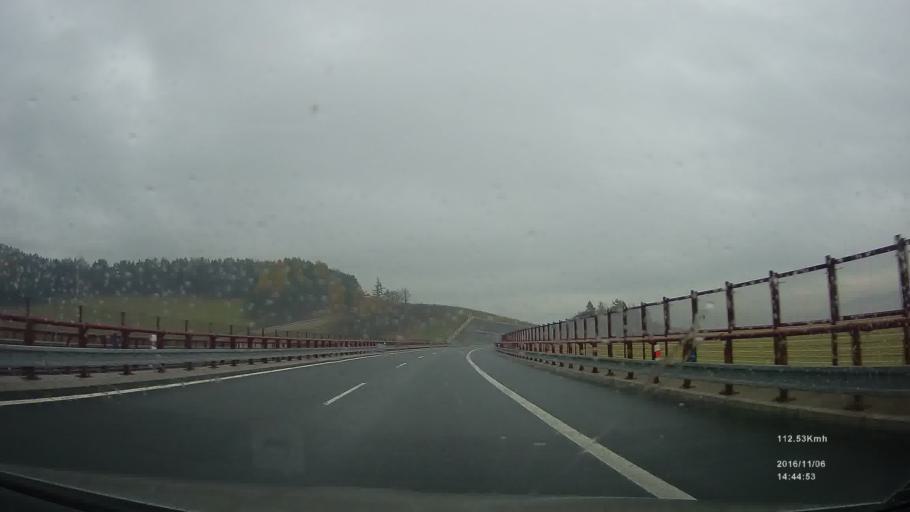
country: SK
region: Presovsky
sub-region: Okres Presov
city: Levoca
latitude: 49.0096
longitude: 20.6636
